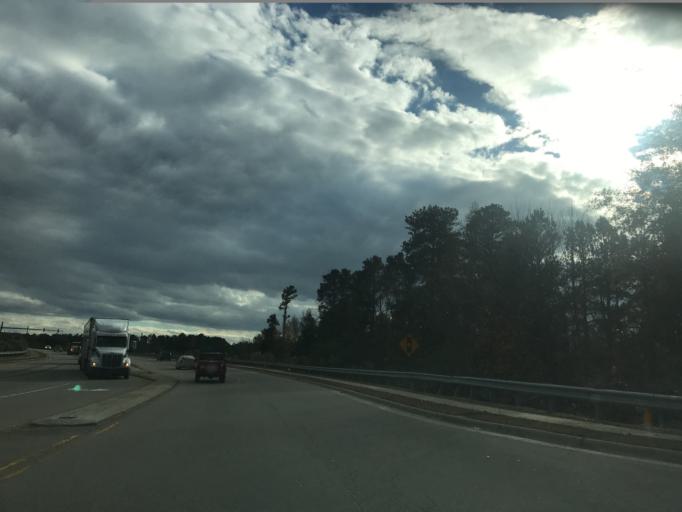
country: US
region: North Carolina
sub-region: Wake County
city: Raleigh
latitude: 35.7807
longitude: -78.5622
